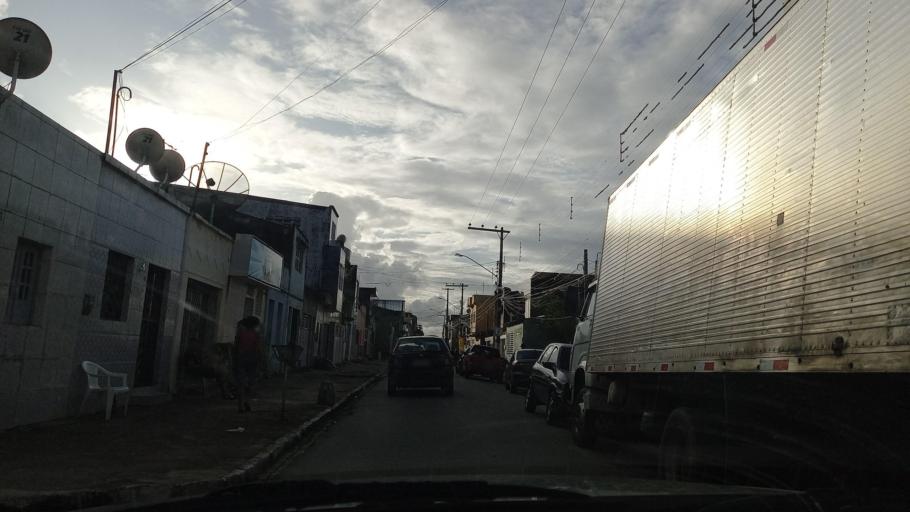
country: BR
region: Pernambuco
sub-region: Palmares
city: Palmares
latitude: -8.6833
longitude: -35.5931
